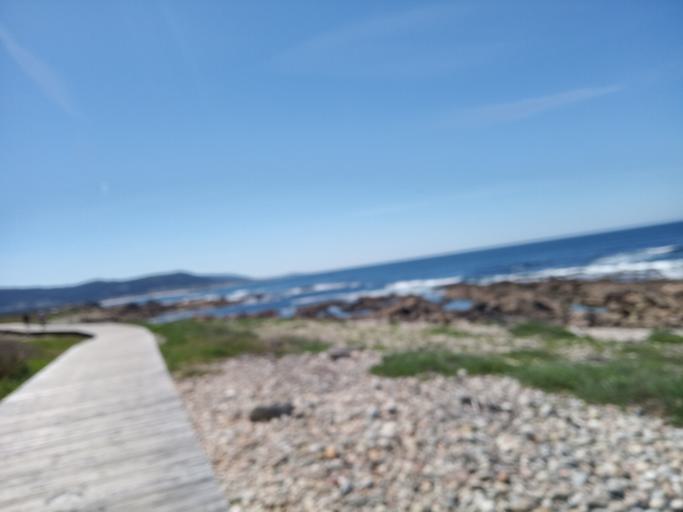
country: ES
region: Galicia
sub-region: Provincia de Pontevedra
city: A Guarda
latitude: 41.8814
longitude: -8.8812
